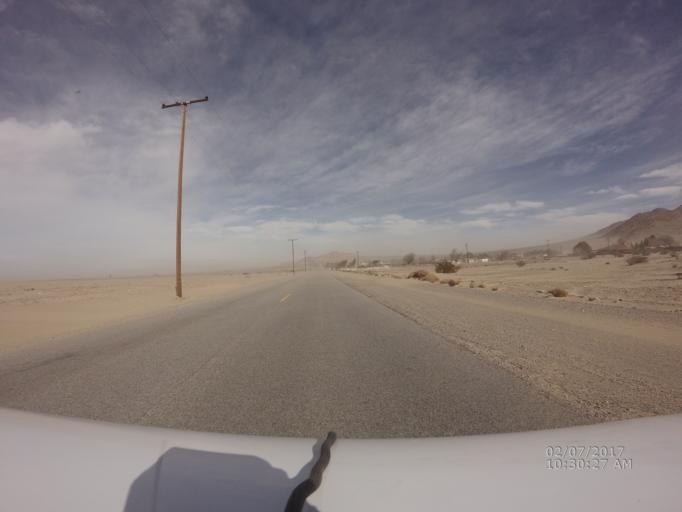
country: US
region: California
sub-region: Los Angeles County
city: Lake Los Angeles
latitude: 34.6627
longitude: -117.8275
